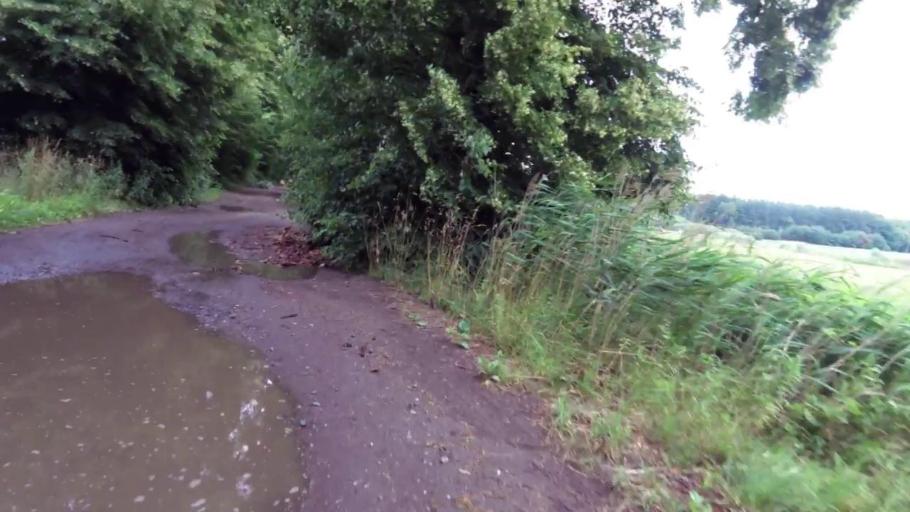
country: PL
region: West Pomeranian Voivodeship
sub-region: Powiat pyrzycki
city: Lipiany
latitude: 52.9703
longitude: 14.9281
